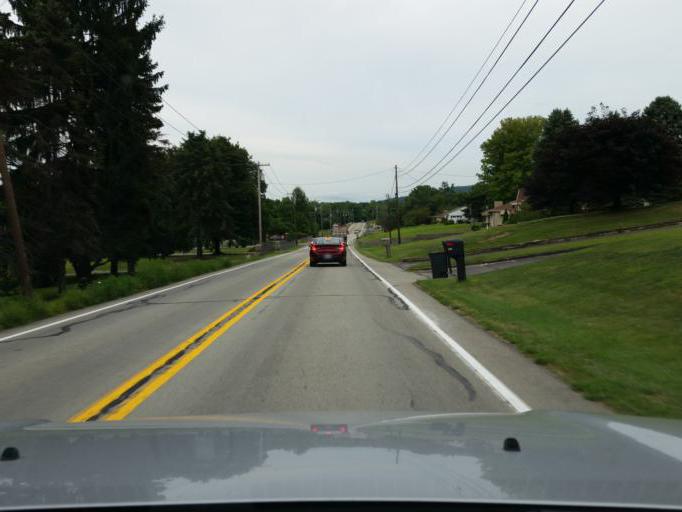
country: US
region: Pennsylvania
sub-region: Westmoreland County
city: Derry
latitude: 40.3172
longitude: -79.3266
